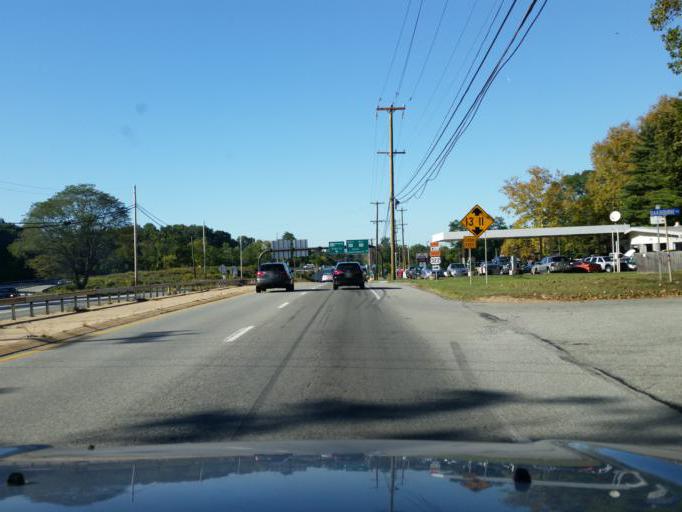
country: US
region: Pennsylvania
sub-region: Chester County
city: West Chester
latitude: 39.9374
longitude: -75.5894
